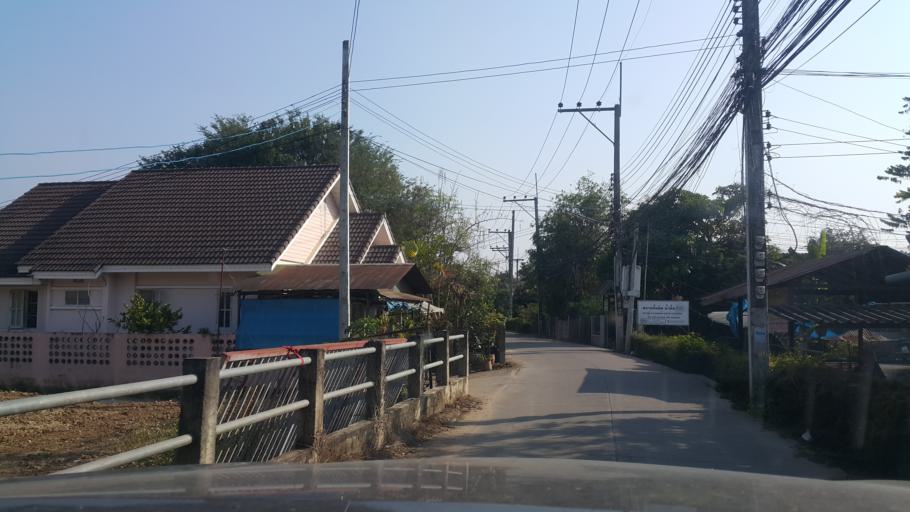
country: TH
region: Chiang Mai
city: Saraphi
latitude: 18.7337
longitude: 99.0242
